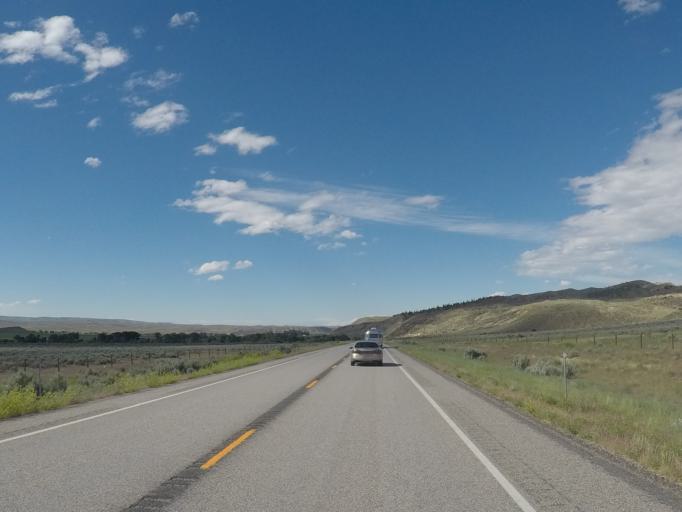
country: US
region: Montana
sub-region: Carbon County
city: Red Lodge
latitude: 45.0057
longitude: -109.0538
